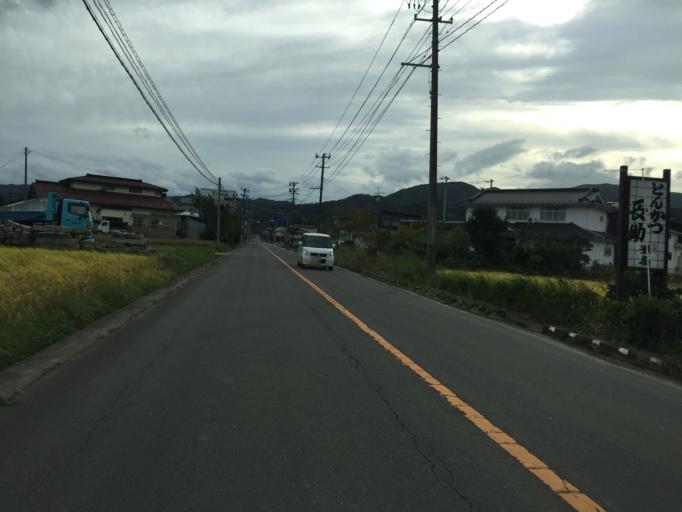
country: JP
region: Miyagi
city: Marumori
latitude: 37.9262
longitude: 140.7711
